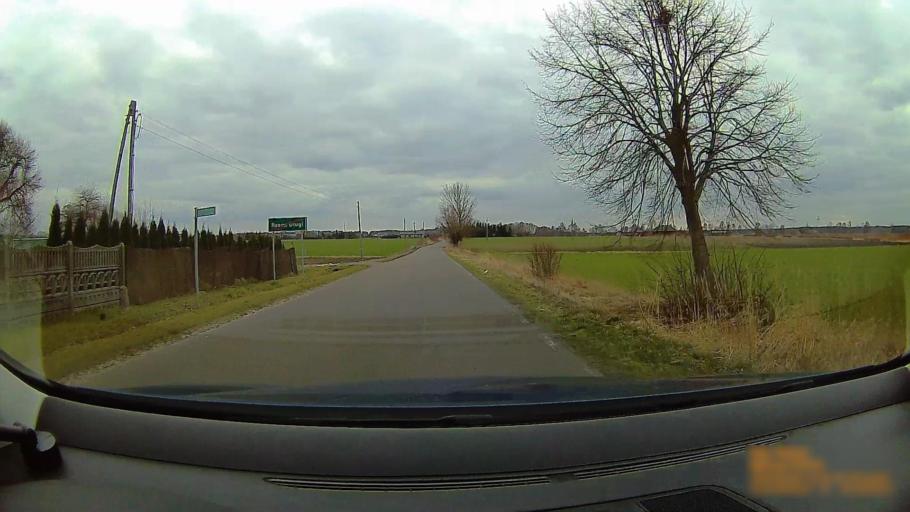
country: PL
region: Greater Poland Voivodeship
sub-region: Powiat koninski
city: Rzgow Pierwszy
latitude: 52.1389
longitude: 18.0566
